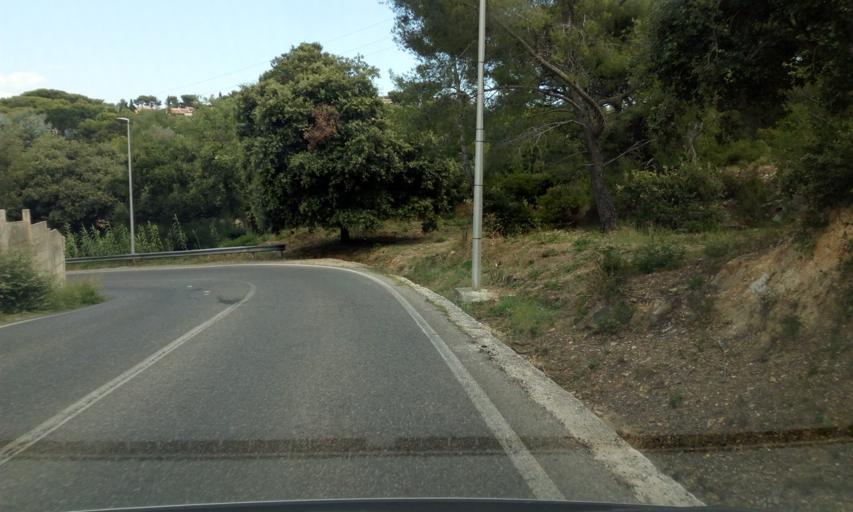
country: FR
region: Provence-Alpes-Cote d'Azur
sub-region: Departement du Var
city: Le Pradet
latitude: 43.0859
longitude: 6.0272
